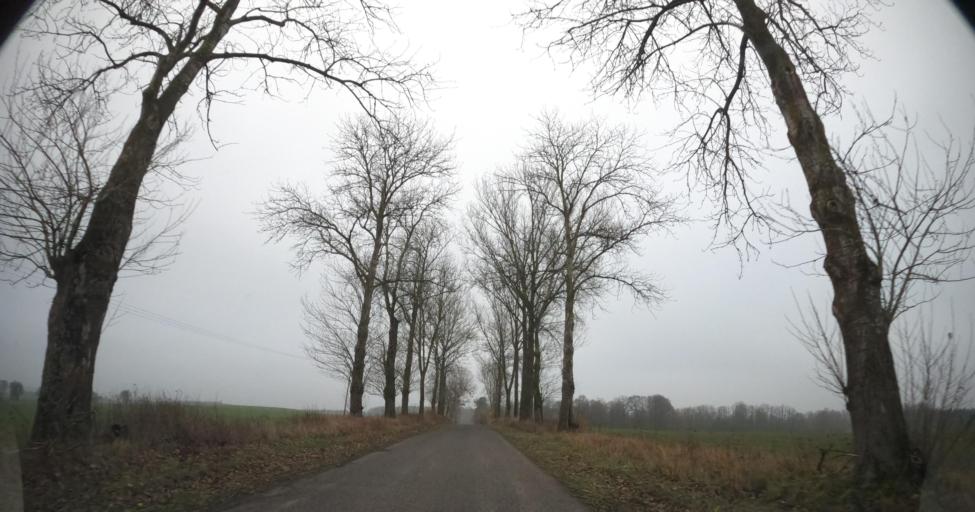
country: PL
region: West Pomeranian Voivodeship
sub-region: Powiat lobeski
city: Wegorzyno
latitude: 53.5432
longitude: 15.6370
